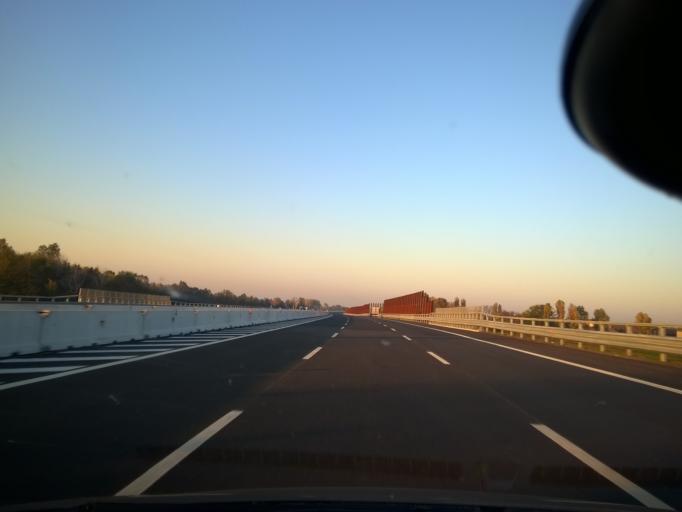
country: IT
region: Lombardy
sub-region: Citta metropolitana di Milano
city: Dresano
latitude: 45.3792
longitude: 9.3754
